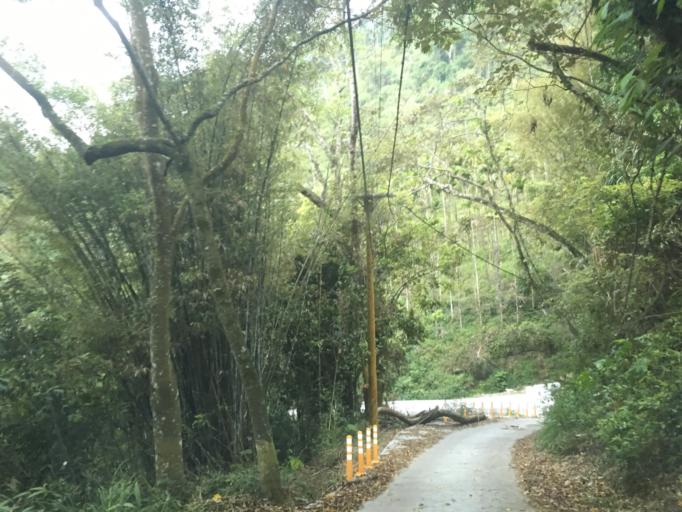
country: TW
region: Taiwan
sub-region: Nantou
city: Puli
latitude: 23.9636
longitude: 120.8407
